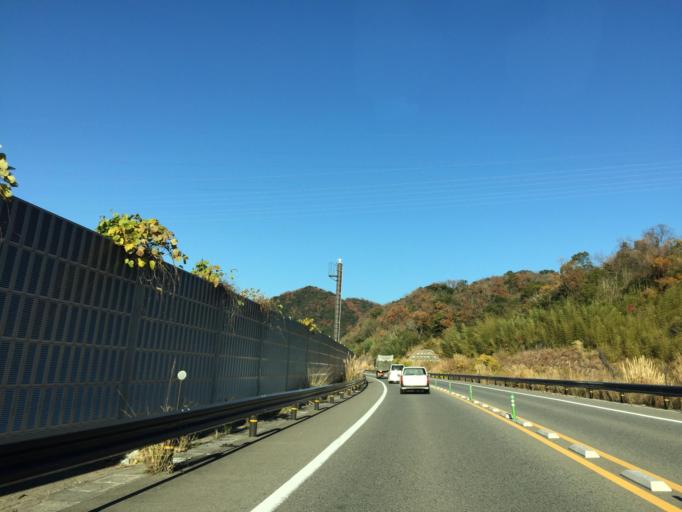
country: JP
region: Wakayama
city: Wakayama-shi
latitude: 34.2603
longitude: 135.1731
